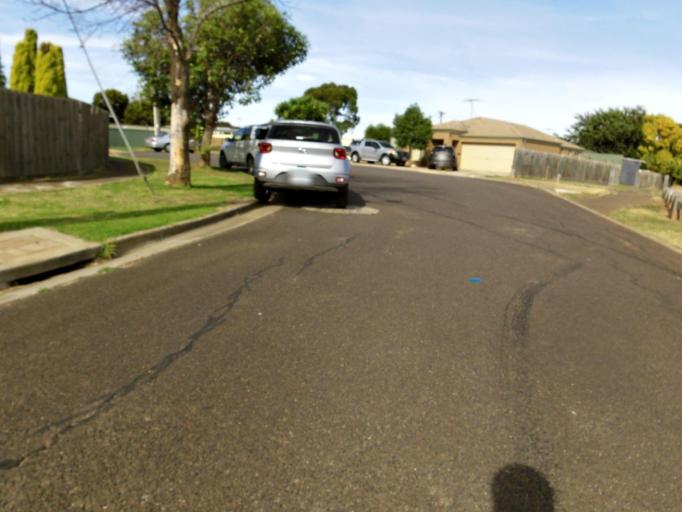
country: AU
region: Victoria
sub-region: Melton
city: Melton West
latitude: -37.6797
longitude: 144.5720
